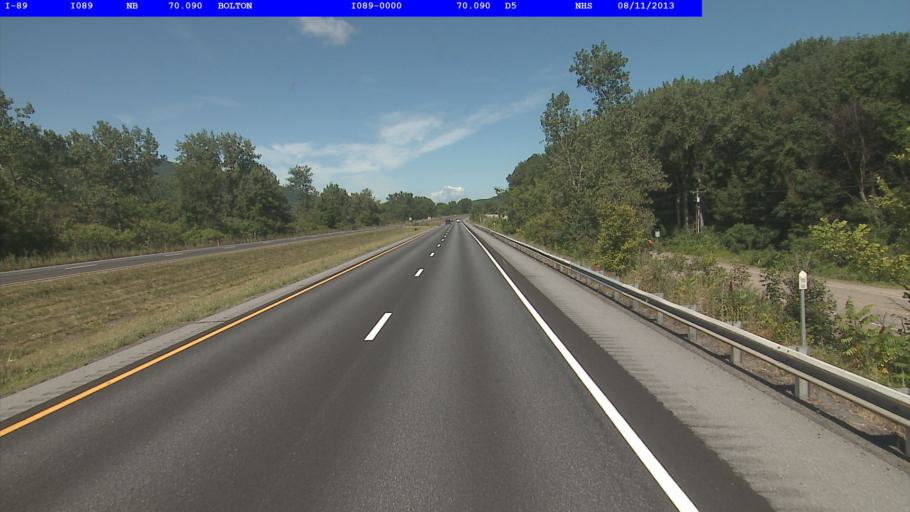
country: US
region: Vermont
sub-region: Washington County
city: Waterbury
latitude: 44.3704
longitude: -72.8698
